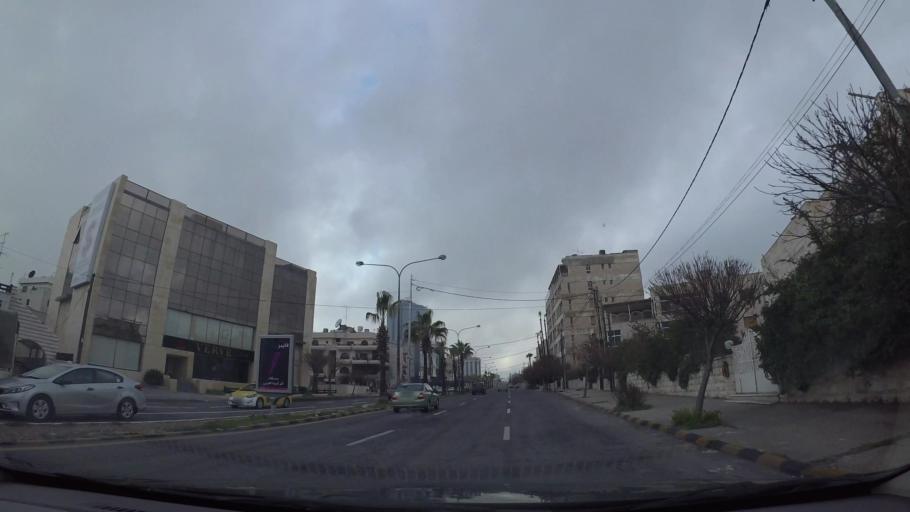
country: JO
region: Amman
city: Wadi as Sir
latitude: 31.9553
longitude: 35.8707
